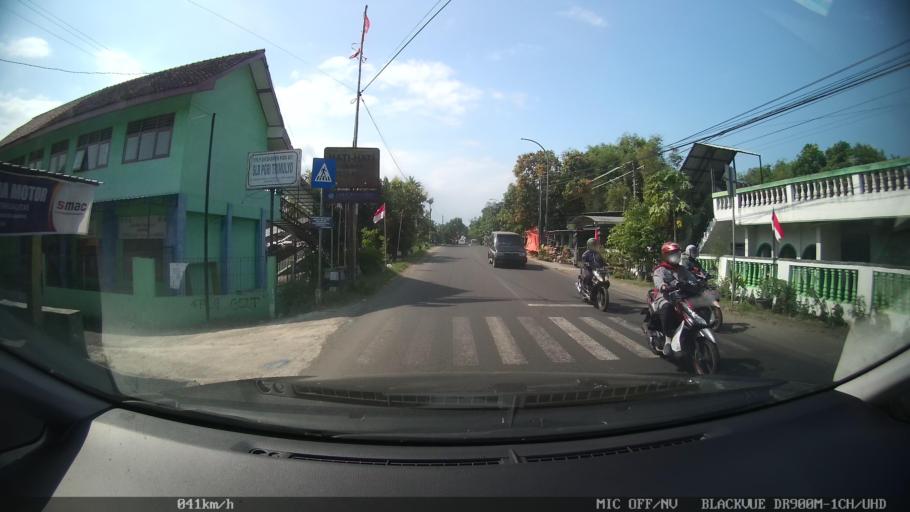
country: ID
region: Daerah Istimewa Yogyakarta
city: Sewon
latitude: -7.8939
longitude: 110.3854
